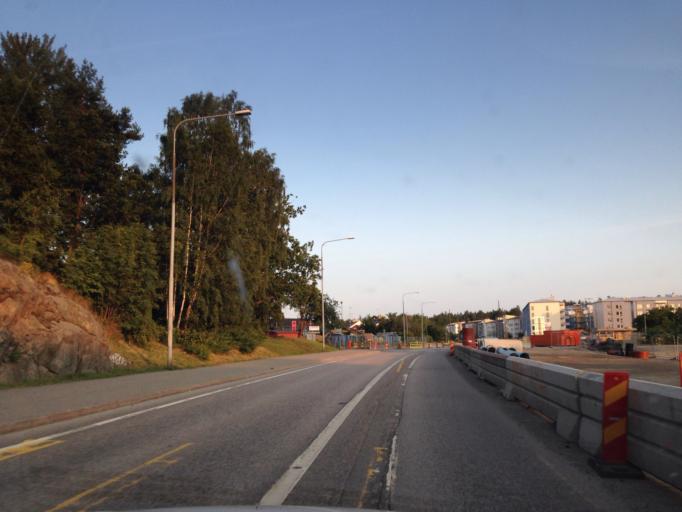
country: SE
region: Stockholm
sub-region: Varmdo Kommun
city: Gustavsberg
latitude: 59.3228
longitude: 18.3865
